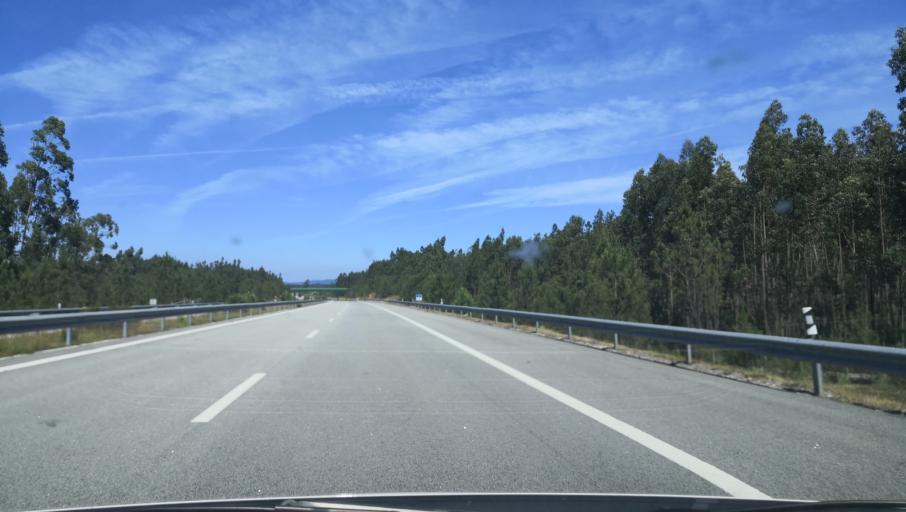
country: PT
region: Coimbra
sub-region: Montemor-O-Velho
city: Arazede
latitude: 40.2746
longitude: -8.5957
